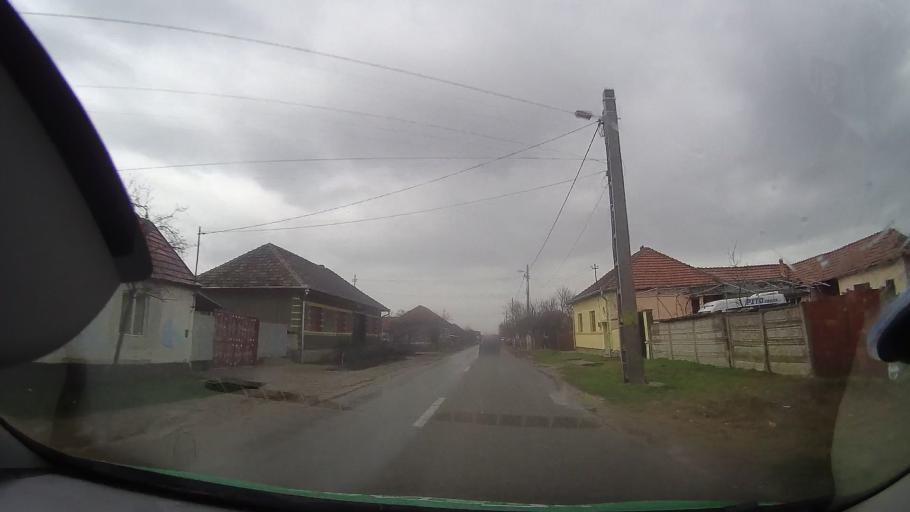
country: RO
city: Capalna
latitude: 46.7027
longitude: 22.0879
